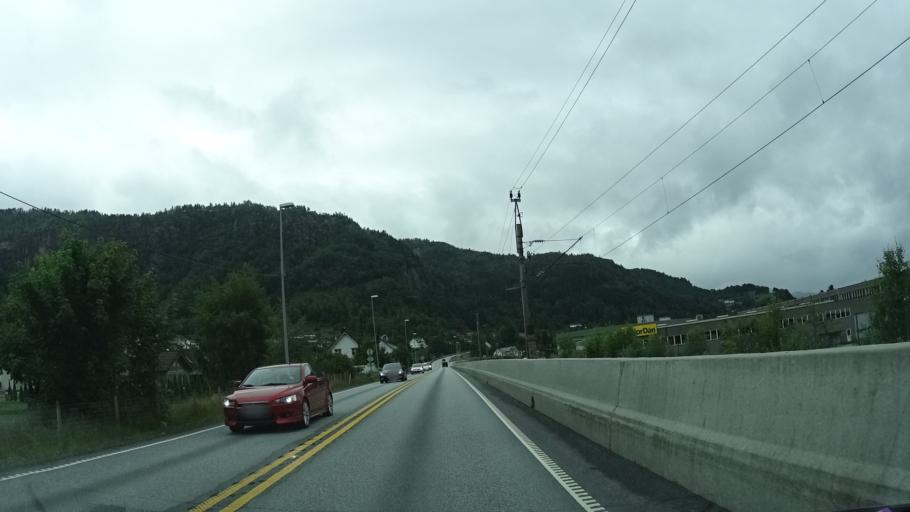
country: NO
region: Rogaland
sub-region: Lund
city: Moi
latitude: 58.4606
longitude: 6.5412
